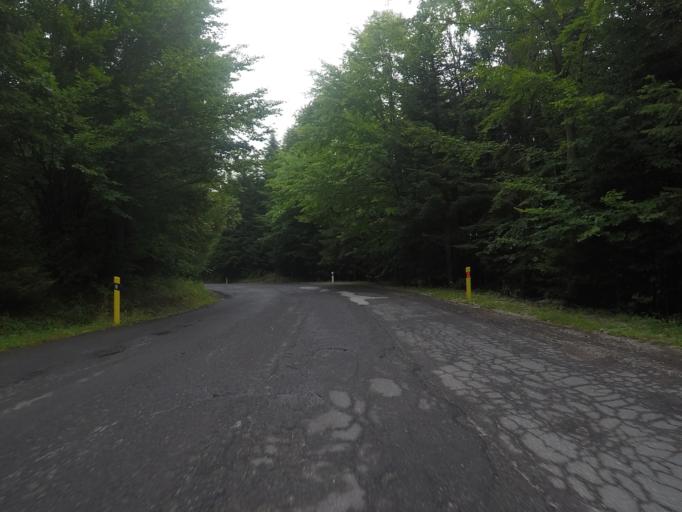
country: SK
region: Kosicky
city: Spisska Nova Ves
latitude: 48.8586
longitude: 20.5206
